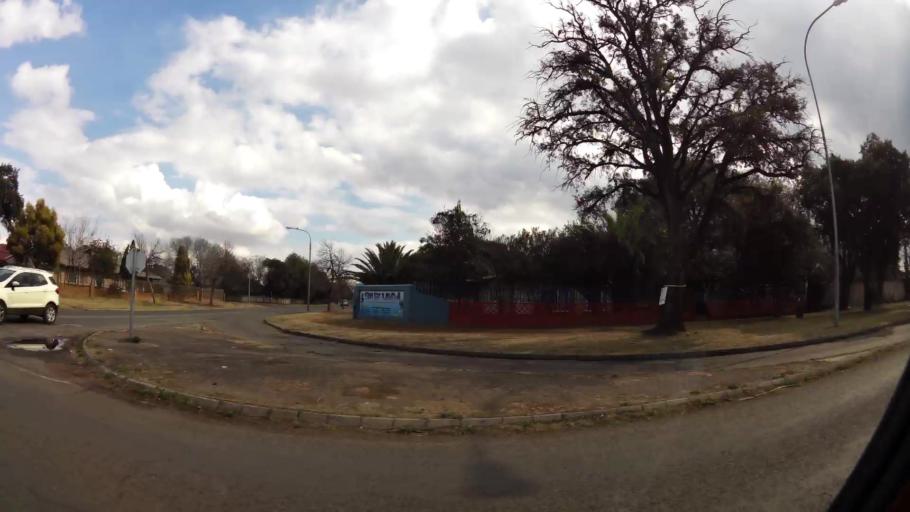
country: ZA
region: Gauteng
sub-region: Sedibeng District Municipality
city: Vanderbijlpark
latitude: -26.7101
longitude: 27.8360
